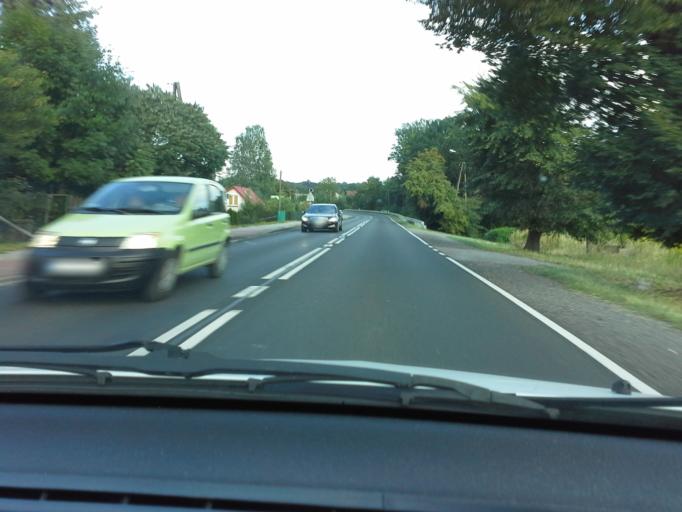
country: PL
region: Lesser Poland Voivodeship
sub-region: Powiat chrzanowski
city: Psary
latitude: 50.1431
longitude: 19.5144
